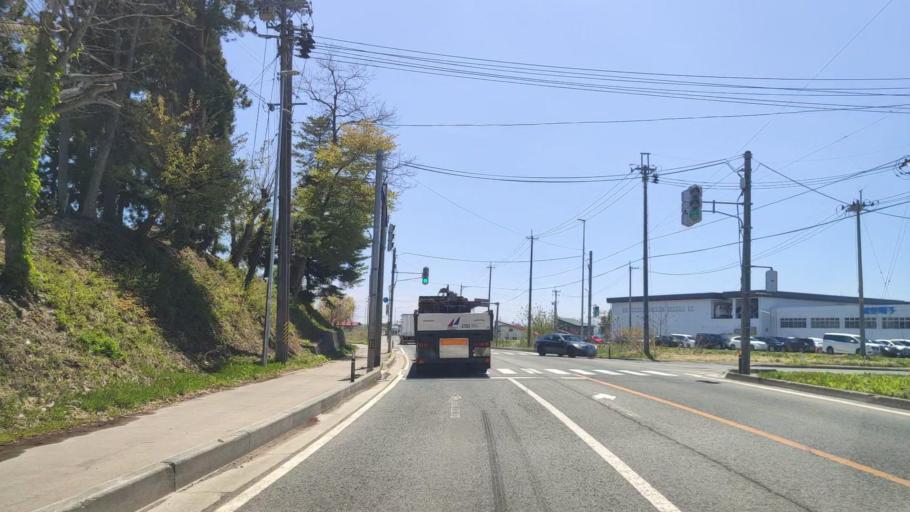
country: JP
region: Yamagata
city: Shinjo
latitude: 38.8223
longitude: 140.3264
